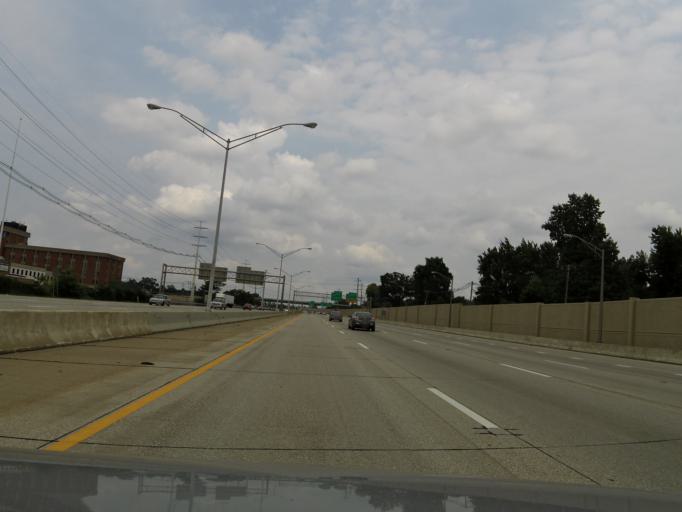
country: US
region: Kentucky
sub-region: Jefferson County
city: Saint Regis Park
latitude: 38.2308
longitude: -85.6315
